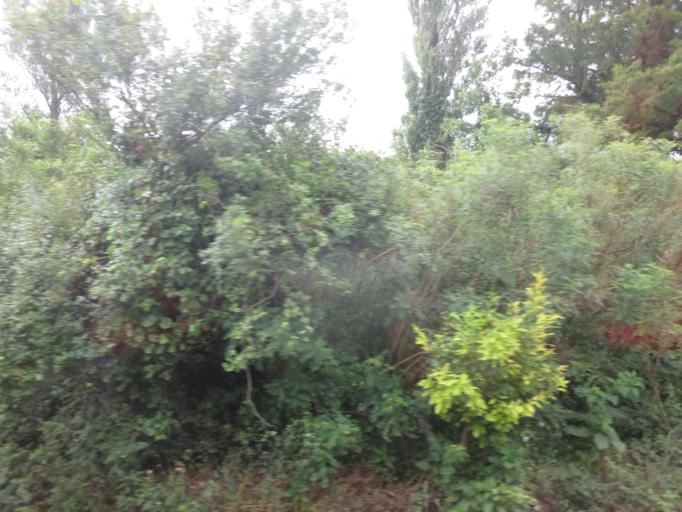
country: GE
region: Imereti
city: K'ulashi
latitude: 42.1875
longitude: 42.4617
